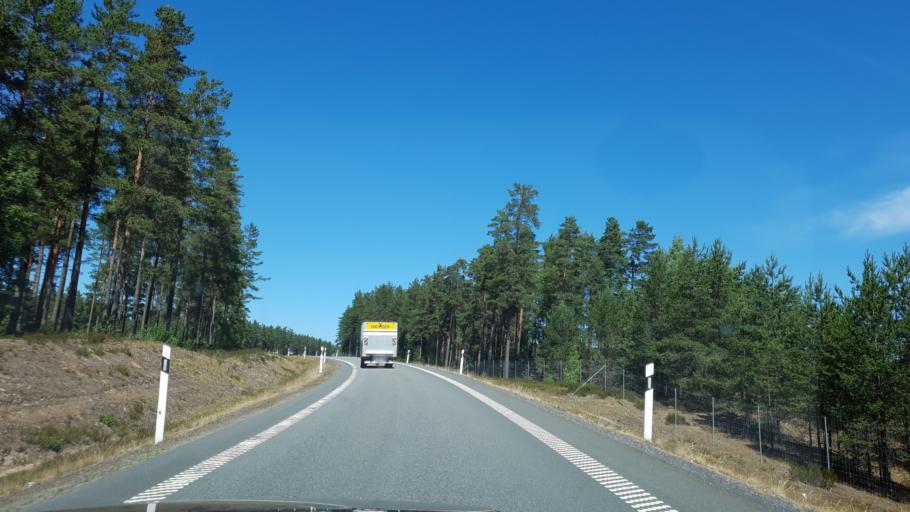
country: SE
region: Joenkoeping
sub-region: Vaggeryds Kommun
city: Vaggeryd
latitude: 57.5290
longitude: 14.1219
